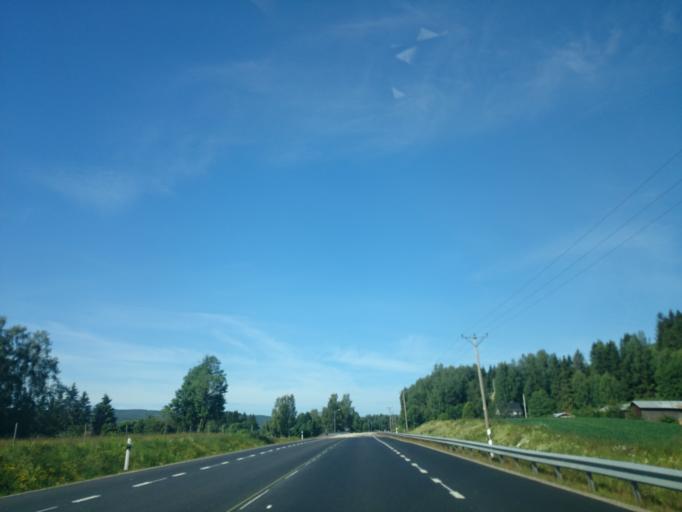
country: SE
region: Vaesternorrland
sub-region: Sundsvalls Kommun
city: Matfors
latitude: 62.3832
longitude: 16.8194
